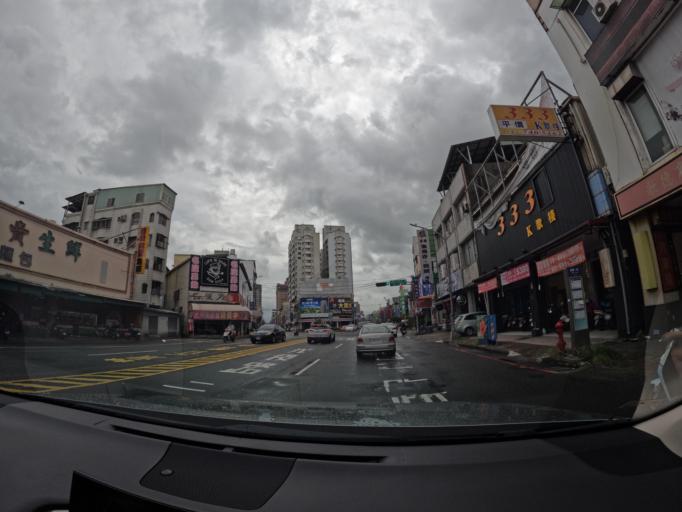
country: TW
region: Taiwan
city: Fengshan
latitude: 22.6295
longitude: 120.3391
